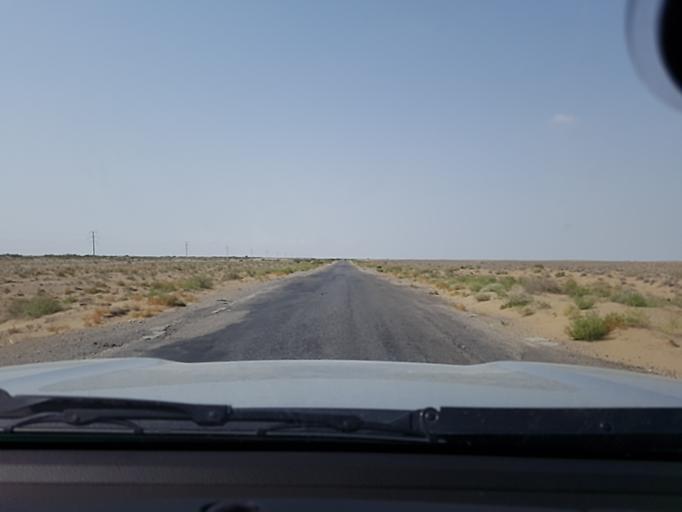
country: TM
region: Balkan
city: Gumdag
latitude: 38.7899
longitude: 54.5976
